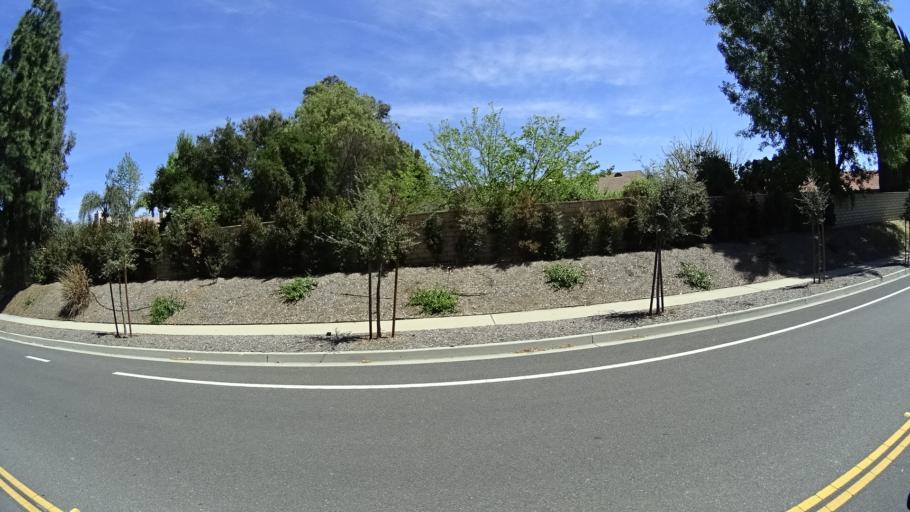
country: US
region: California
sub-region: Ventura County
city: Thousand Oaks
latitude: 34.2200
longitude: -118.8756
